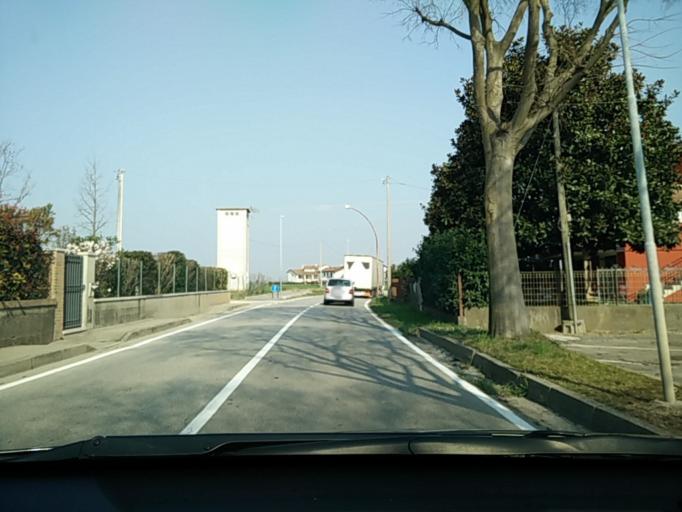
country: IT
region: Veneto
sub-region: Provincia di Treviso
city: Postioma
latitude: 45.7206
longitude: 12.1554
